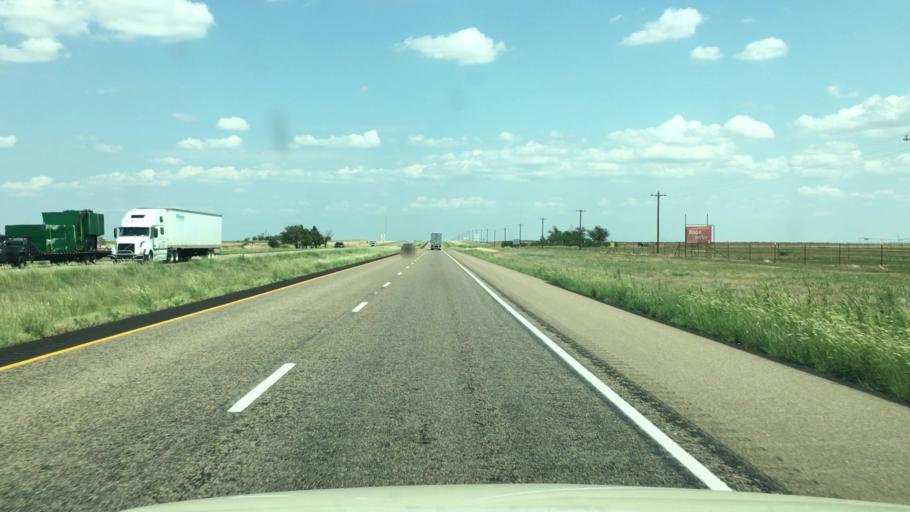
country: US
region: Texas
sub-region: Armstrong County
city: Claude
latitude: 35.0338
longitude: -101.1806
